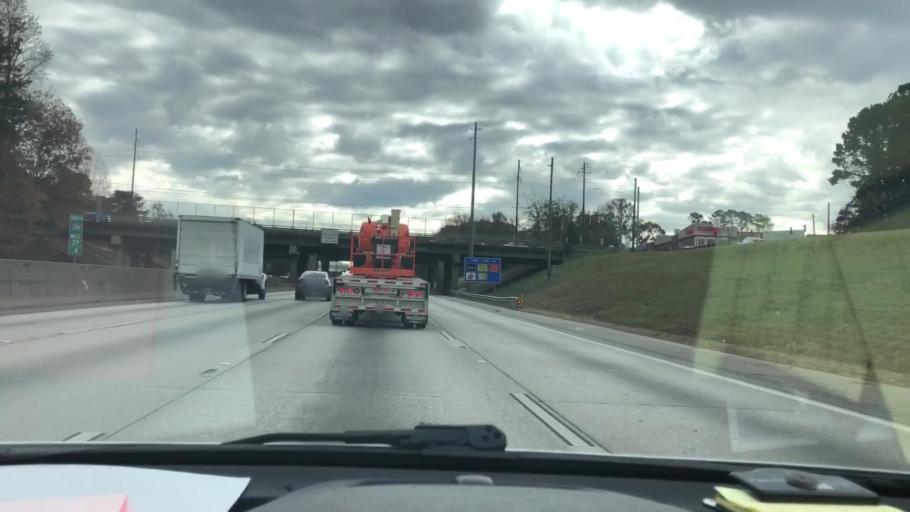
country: US
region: Georgia
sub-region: DeKalb County
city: Clarkston
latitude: 33.8036
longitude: -84.2511
